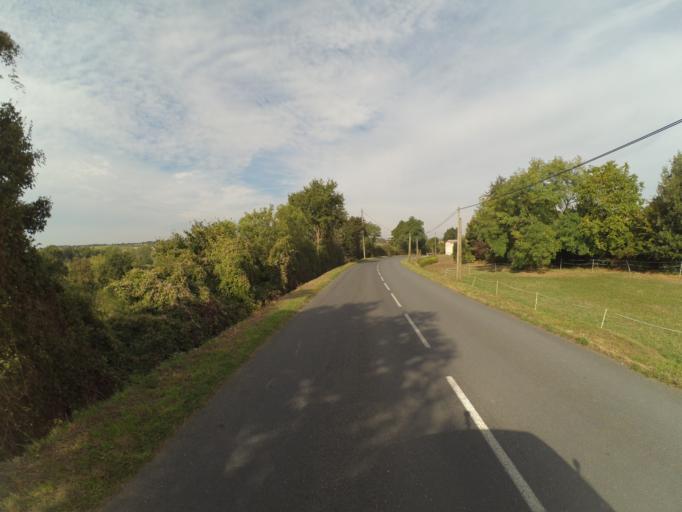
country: FR
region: Pays de la Loire
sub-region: Departement de Maine-et-Loire
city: La Chapelle-du-Genet
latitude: 47.1834
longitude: -1.0267
